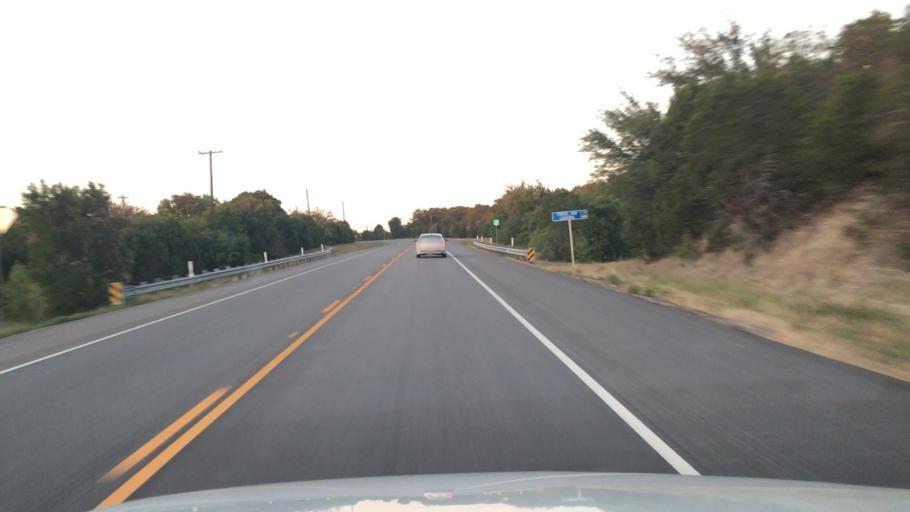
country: US
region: Texas
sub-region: Somervell County
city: Glen Rose
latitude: 32.1943
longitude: -97.8150
